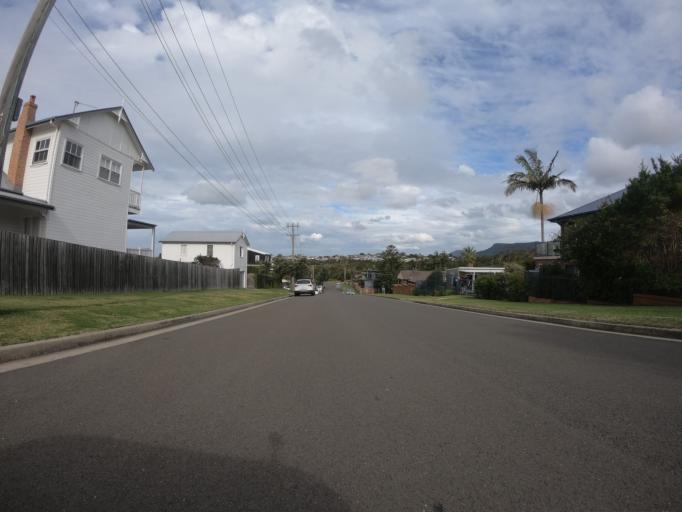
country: AU
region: New South Wales
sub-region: Wollongong
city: Bulli
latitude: -34.3221
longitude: 150.9241
